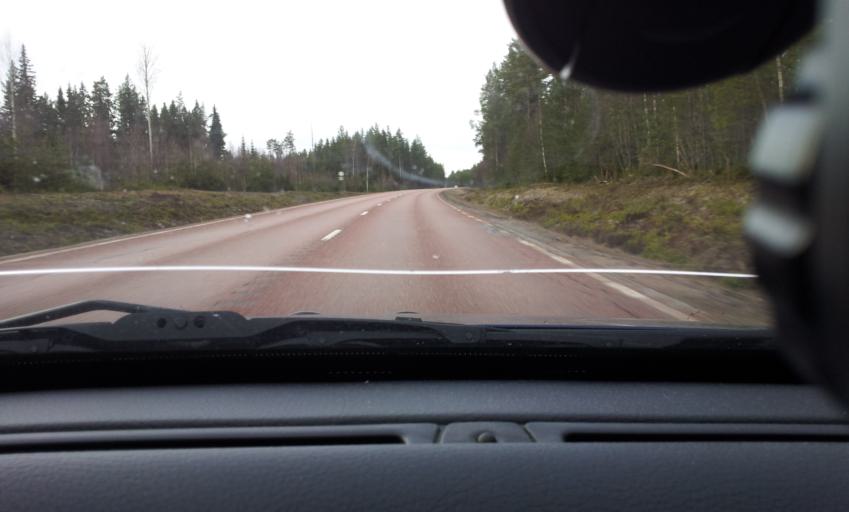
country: SE
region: Gaevleborg
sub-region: Ljusdals Kommun
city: Farila
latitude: 61.8199
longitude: 15.7578
